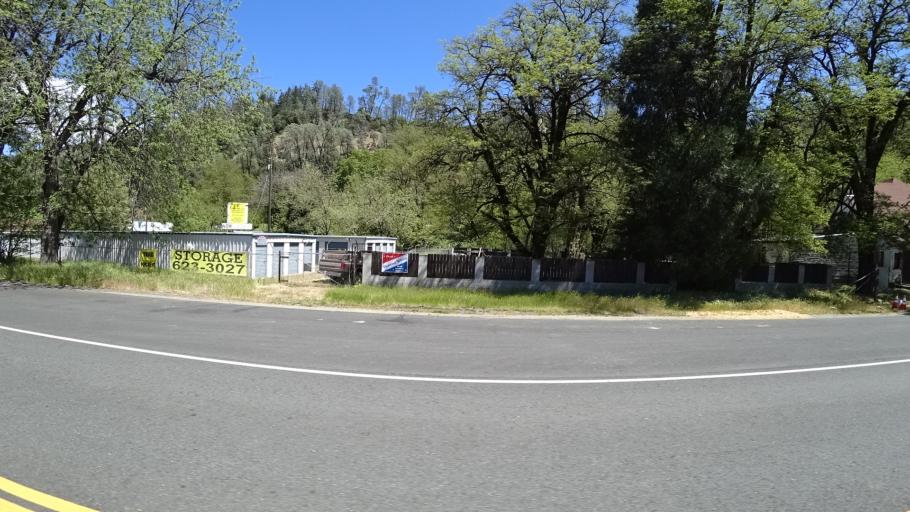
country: US
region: California
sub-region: Trinity County
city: Weaverville
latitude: 40.7308
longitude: -123.0546
